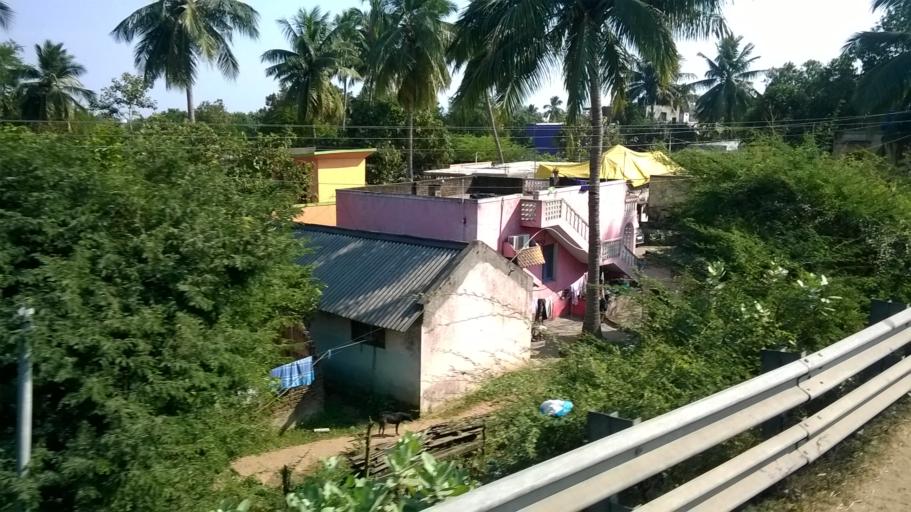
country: IN
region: Tamil Nadu
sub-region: Kancheepuram
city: Wallajahbad
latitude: 12.7960
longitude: 79.8230
